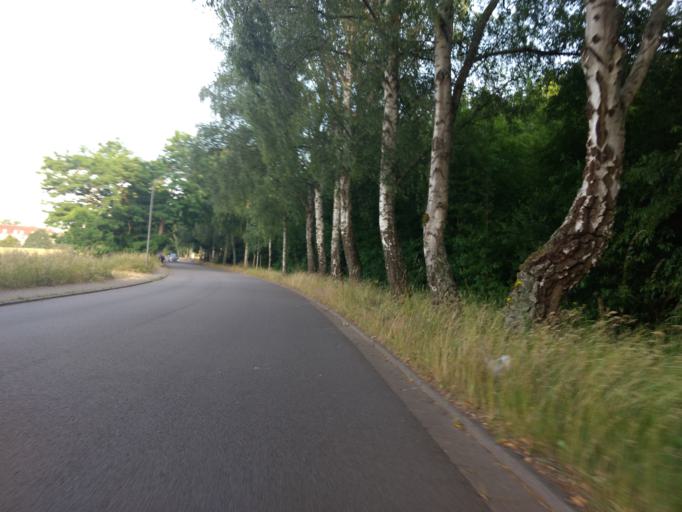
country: DE
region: Saarland
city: Saarlouis
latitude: 49.3063
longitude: 6.7283
